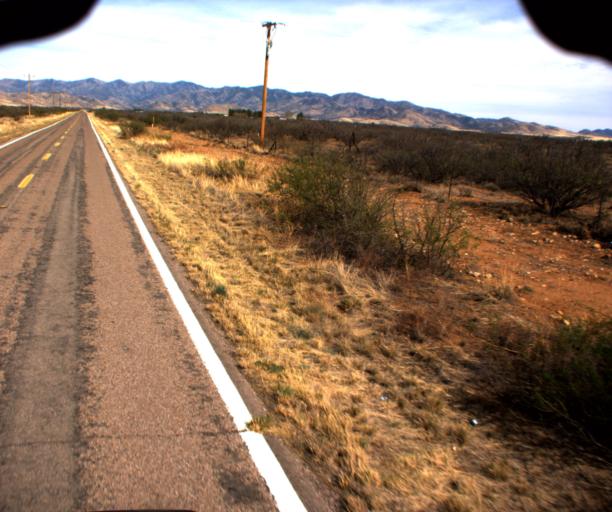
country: US
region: Arizona
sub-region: Cochise County
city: Willcox
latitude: 31.8760
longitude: -109.5260
